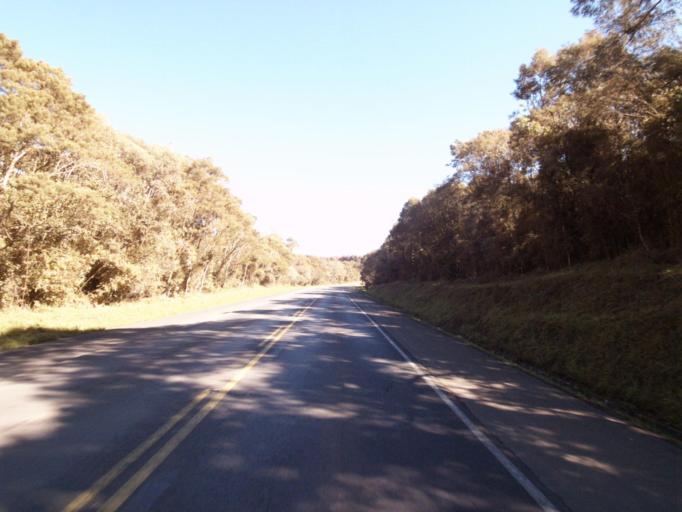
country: BR
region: Santa Catarina
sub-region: Concordia
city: Concordia
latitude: -26.9728
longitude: -51.8389
